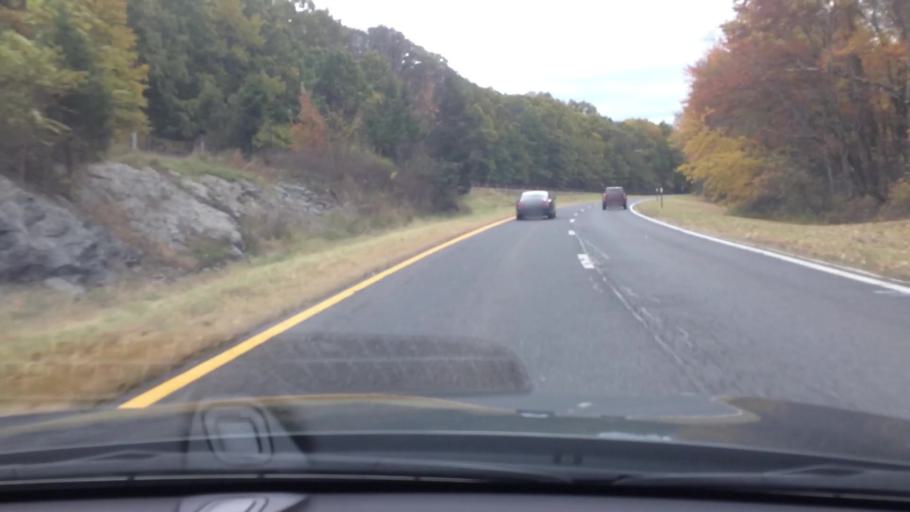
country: US
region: New York
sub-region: Dutchess County
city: Pleasant Valley
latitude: 41.7903
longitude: -73.7706
